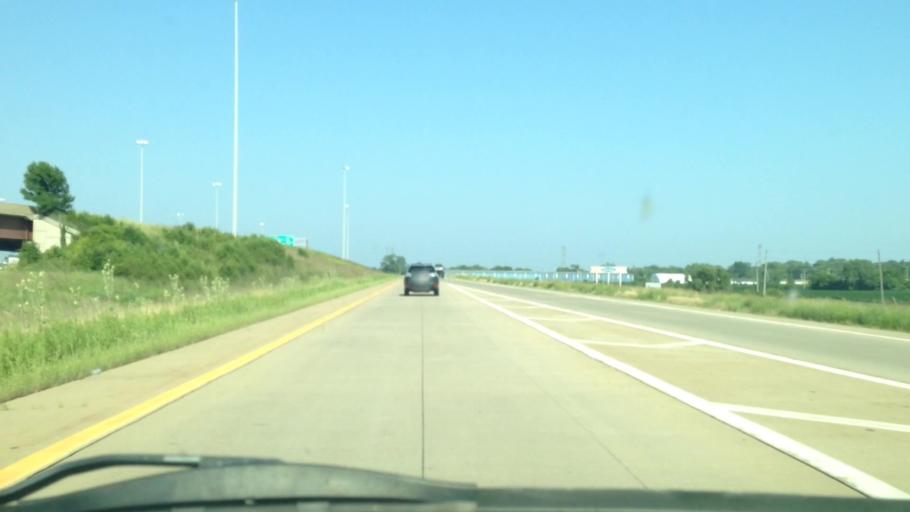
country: US
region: Illinois
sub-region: Cook County
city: Thornton
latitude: 41.5773
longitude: -87.5771
